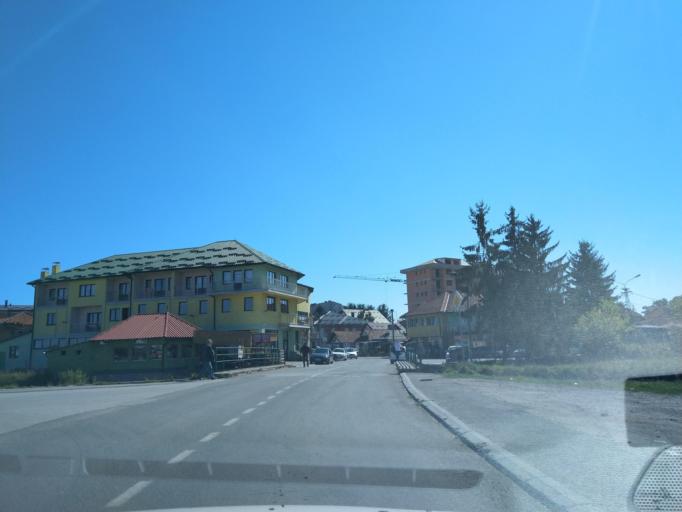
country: RS
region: Central Serbia
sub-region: Zlatiborski Okrug
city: Sjenica
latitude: 43.2753
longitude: 20.0026
